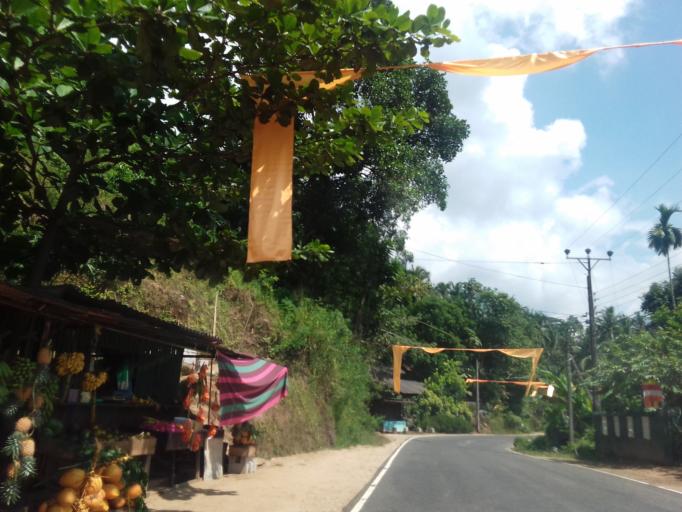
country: LK
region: Central
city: Hatton
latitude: 6.9969
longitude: 80.3573
